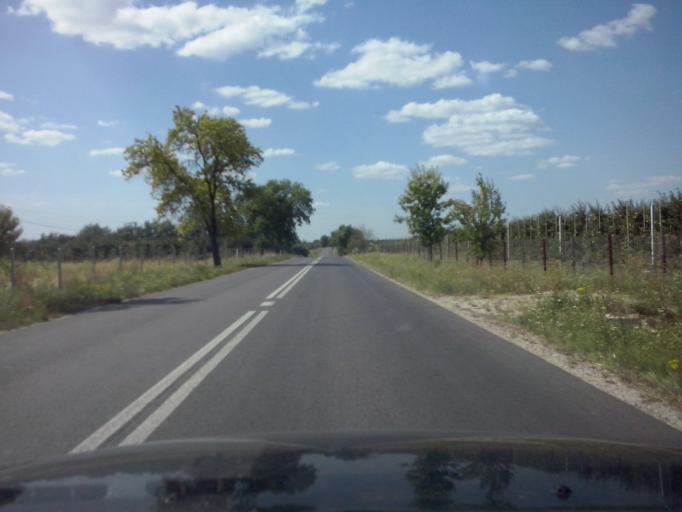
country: PL
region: Swietokrzyskie
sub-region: Powiat staszowski
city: Szydlow
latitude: 50.5870
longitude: 20.9828
